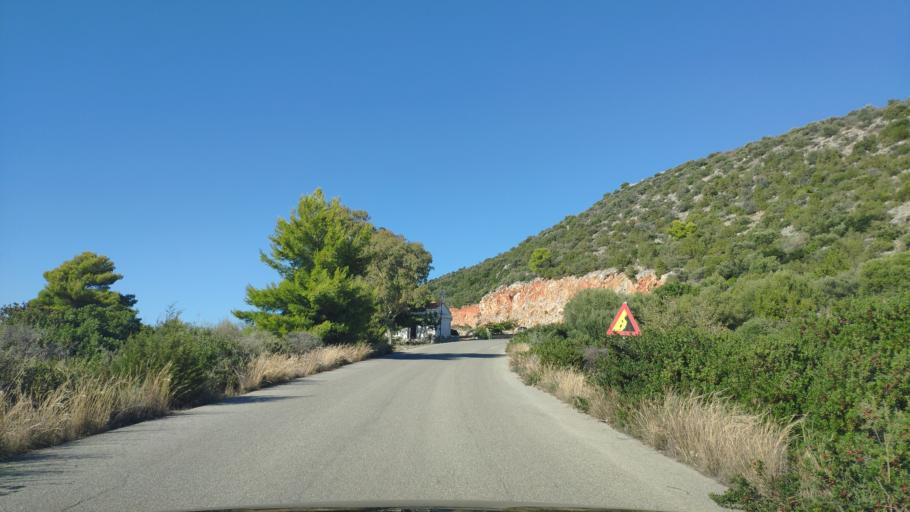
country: GR
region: Attica
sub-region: Nomos Piraios
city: Galatas
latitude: 37.5611
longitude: 23.3641
